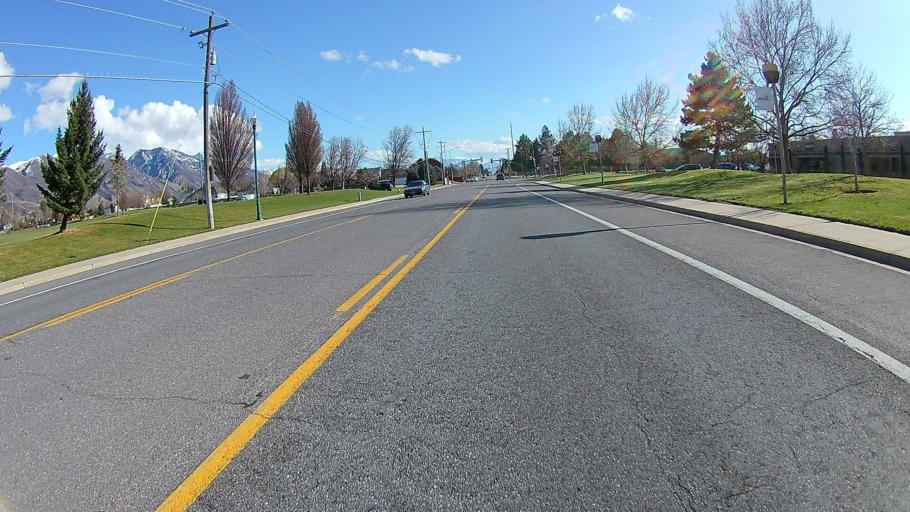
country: US
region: Utah
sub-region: Utah County
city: Orem
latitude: 40.3207
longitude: -111.6768
